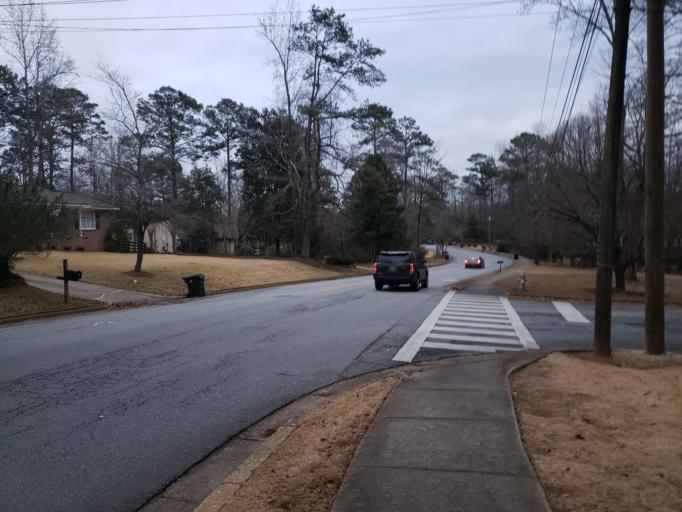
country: US
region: Alabama
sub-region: Lee County
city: Auburn
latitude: 32.5989
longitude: -85.4557
